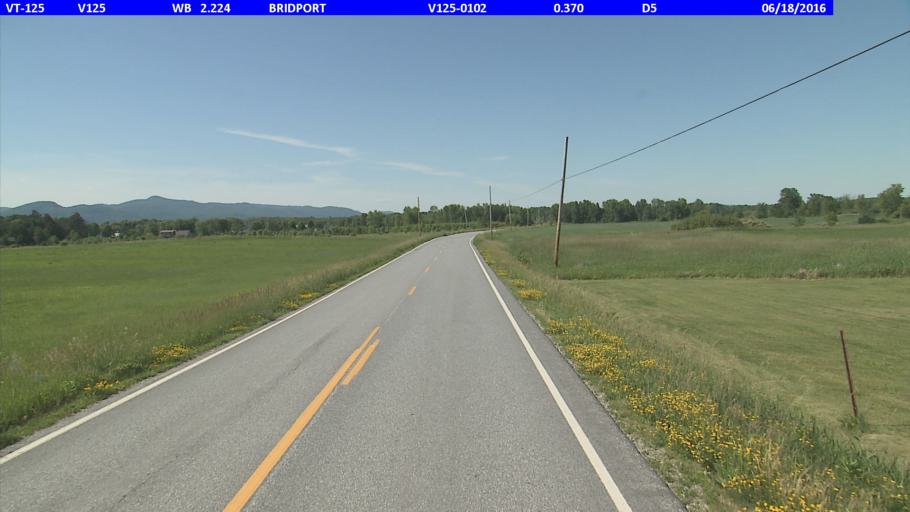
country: US
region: New York
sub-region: Essex County
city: Port Henry
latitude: 44.0167
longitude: -73.3896
